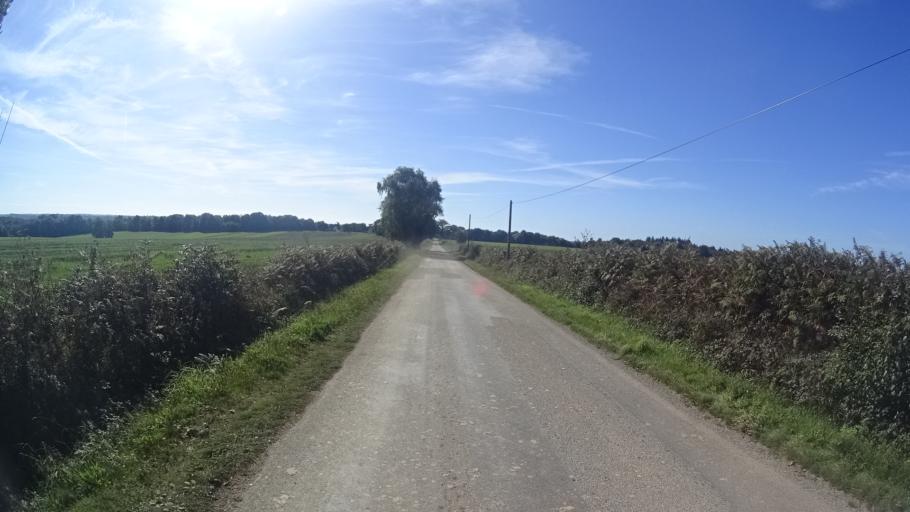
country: FR
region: Brittany
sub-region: Departement du Morbihan
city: La Gacilly
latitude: 47.7449
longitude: -2.1724
